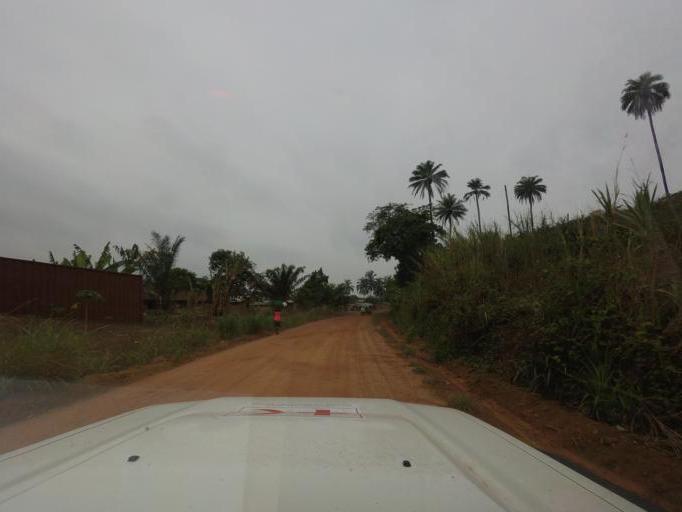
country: LR
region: Lofa
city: Voinjama
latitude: 8.3975
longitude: -9.7871
